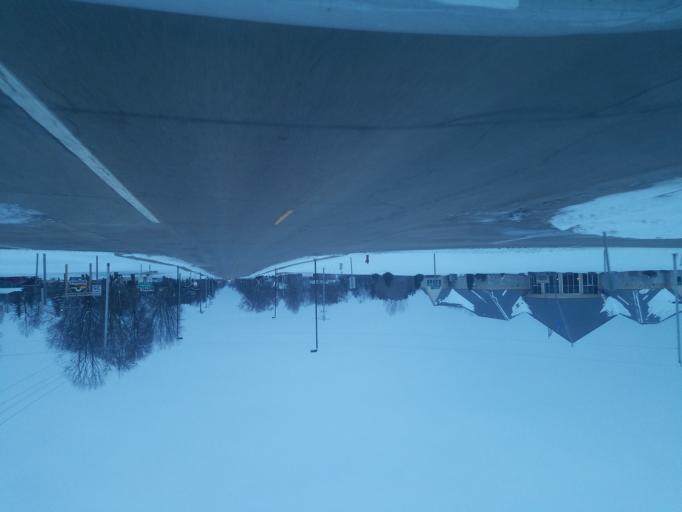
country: US
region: Wisconsin
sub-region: Waupaca County
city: Manawa
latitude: 44.4759
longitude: -88.9204
